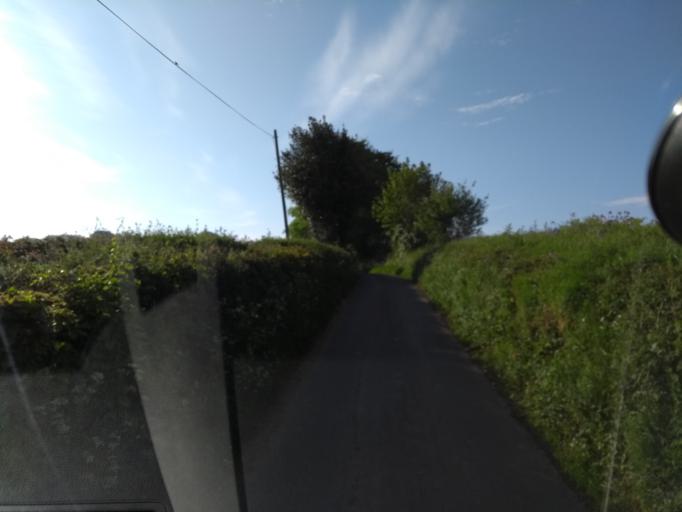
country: GB
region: England
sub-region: Devon
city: Axminster
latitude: 50.7944
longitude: -2.9442
